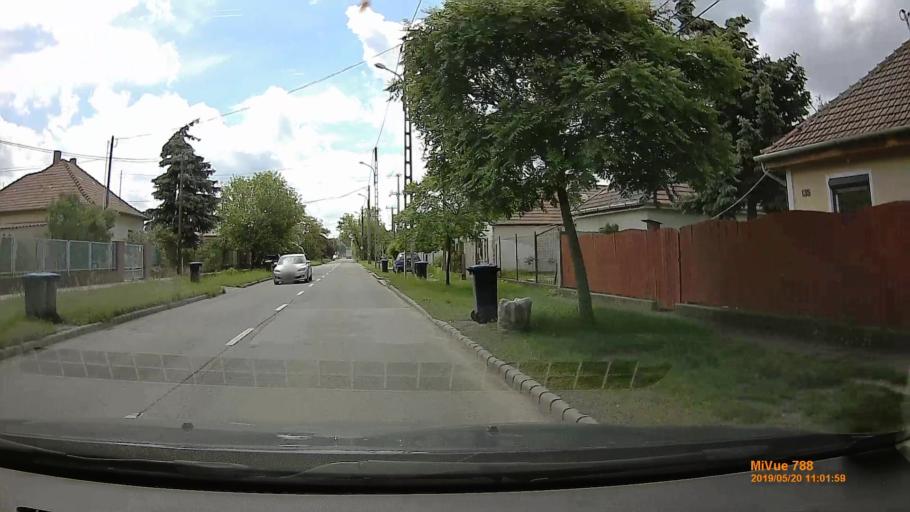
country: HU
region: Budapest
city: Budapest XVII. keruelet
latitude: 47.4763
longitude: 19.2931
